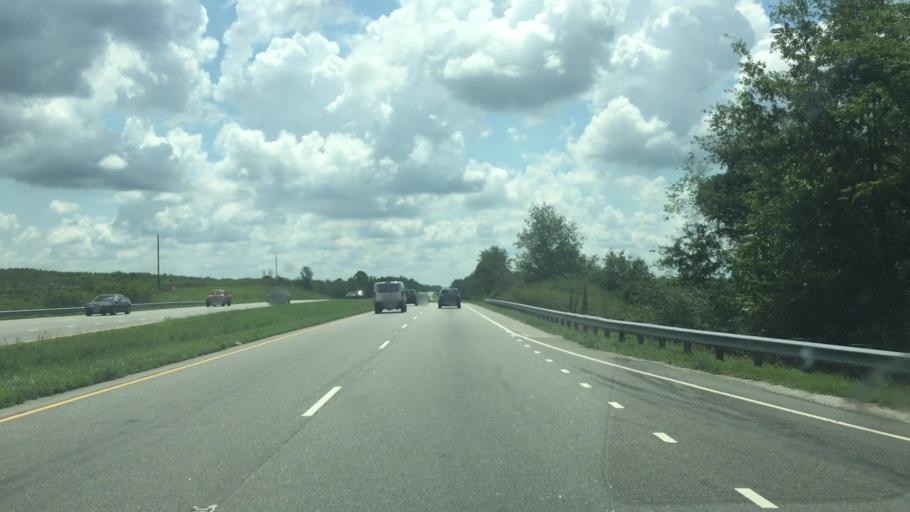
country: US
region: North Carolina
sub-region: Scotland County
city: Laurel Hill
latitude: 34.8503
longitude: -79.6173
